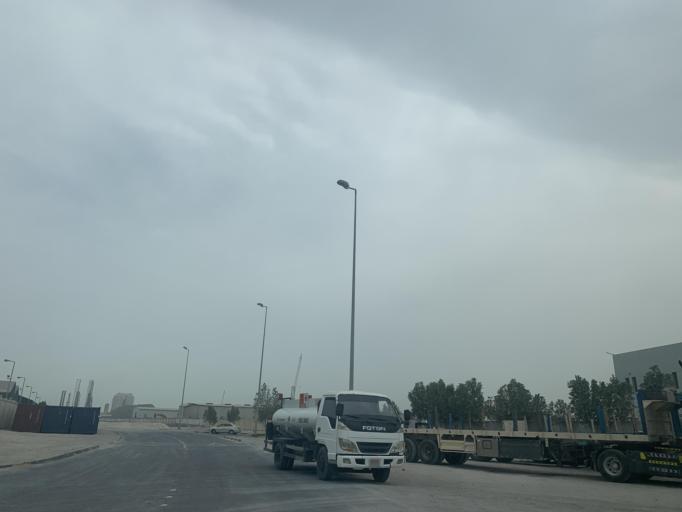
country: BH
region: Muharraq
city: Al Hadd
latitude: 26.2105
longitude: 50.6674
